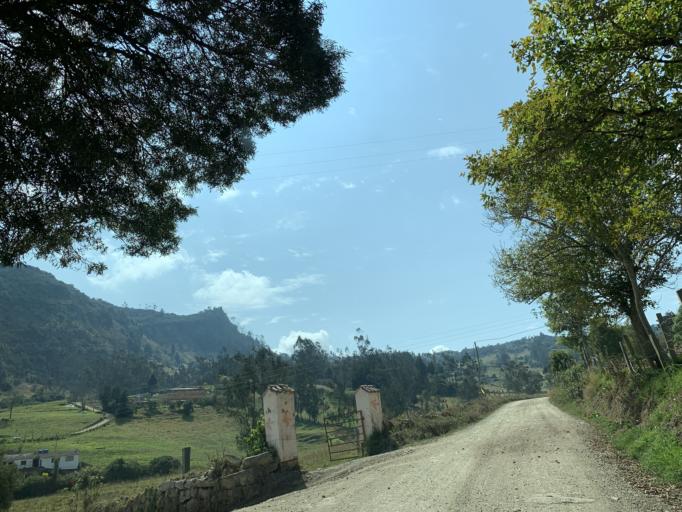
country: CO
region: Boyaca
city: Turmeque
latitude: 5.2830
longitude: -73.4989
